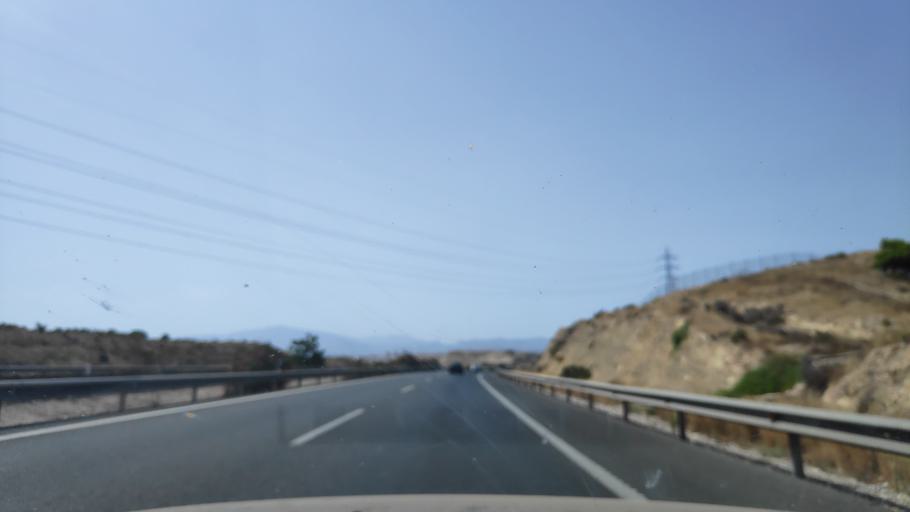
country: ES
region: Murcia
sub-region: Murcia
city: Molina de Segura
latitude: 38.0484
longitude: -1.1721
